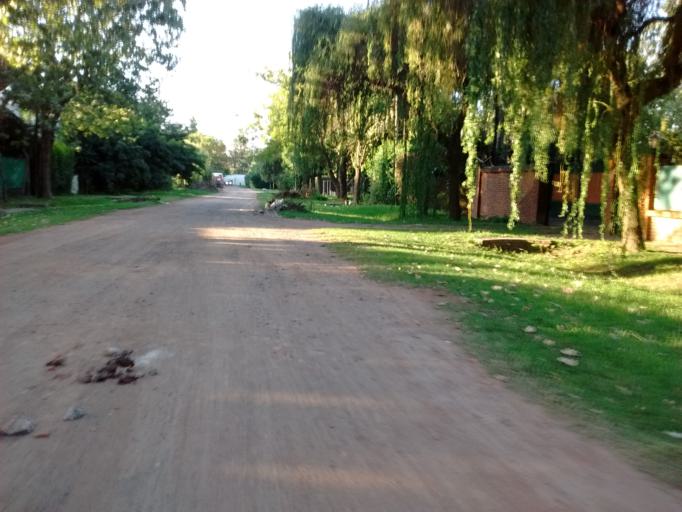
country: AR
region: Santa Fe
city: Funes
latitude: -32.9214
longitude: -60.8286
